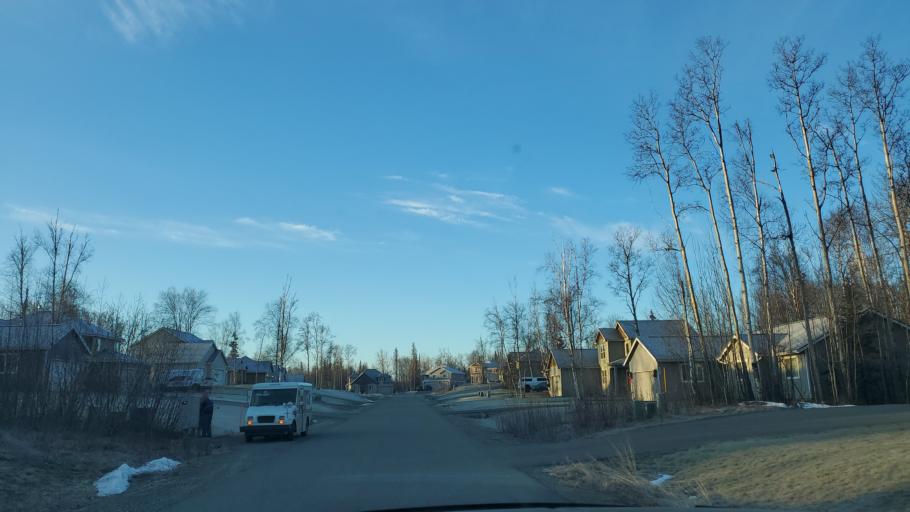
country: US
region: Alaska
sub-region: Matanuska-Susitna Borough
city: Wasilla
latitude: 61.5916
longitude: -149.4526
